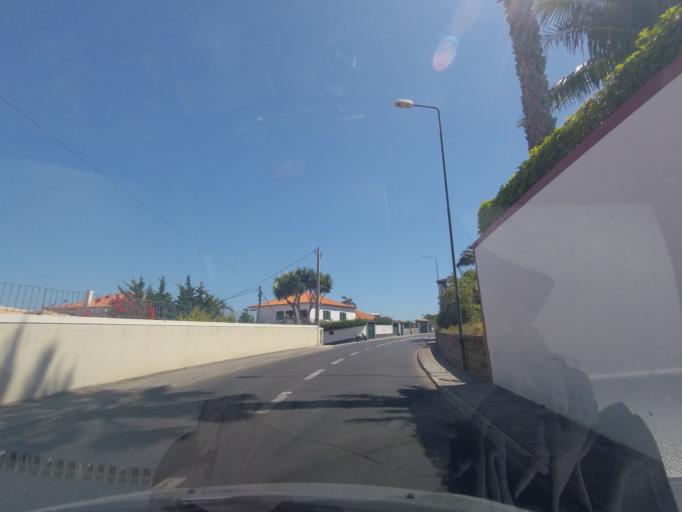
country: PT
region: Madeira
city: Camara de Lobos
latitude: 32.6519
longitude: -16.9346
